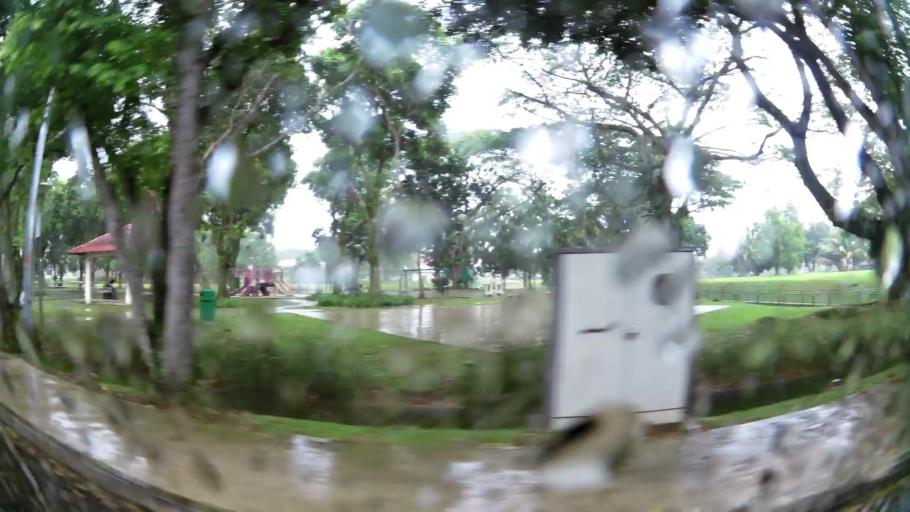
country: MY
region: Johor
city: Kampung Pasir Gudang Baru
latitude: 1.3896
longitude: 103.8518
